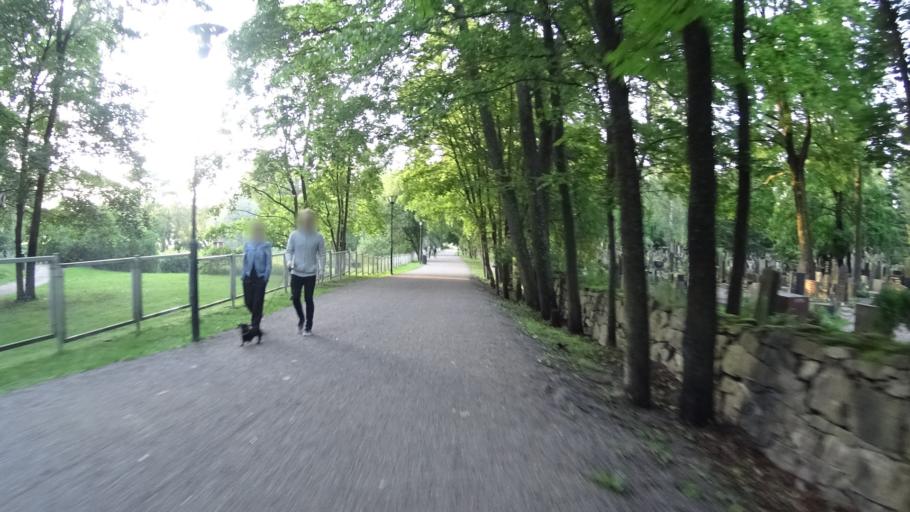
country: FI
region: Uusimaa
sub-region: Helsinki
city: Helsinki
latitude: 60.1671
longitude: 24.9165
